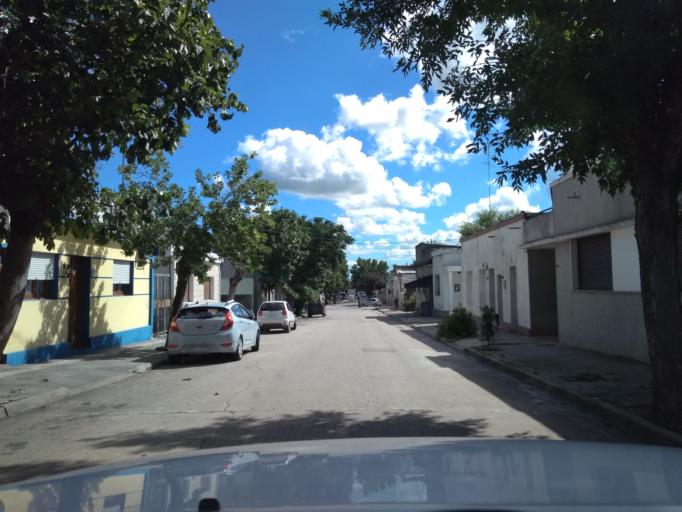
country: UY
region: Florida
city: Florida
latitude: -34.1023
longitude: -56.2156
